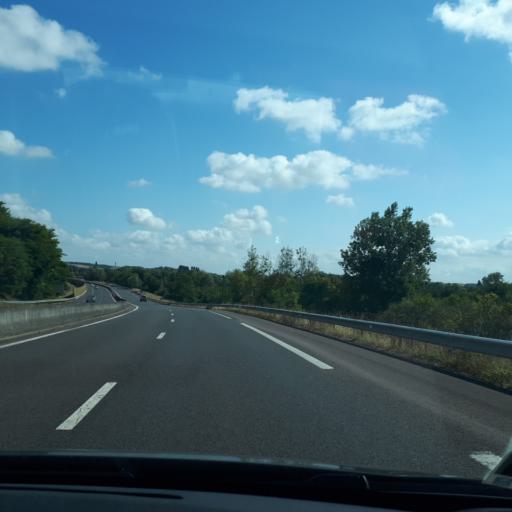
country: FR
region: Centre
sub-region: Departement du Loir-et-Cher
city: Moree
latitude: 47.8754
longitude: 1.1563
